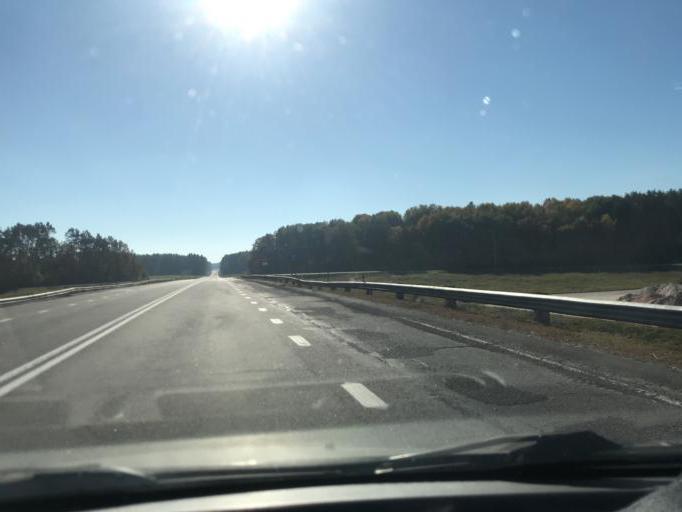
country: BY
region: Gomel
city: Gomel
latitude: 52.3869
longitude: 30.8278
